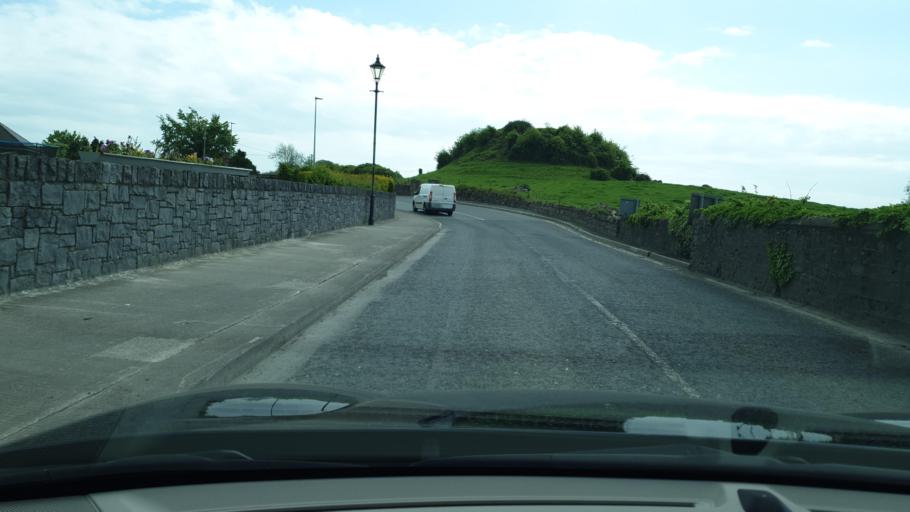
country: IE
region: Ulster
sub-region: An Cabhan
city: Kingscourt
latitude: 53.8241
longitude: -6.7540
